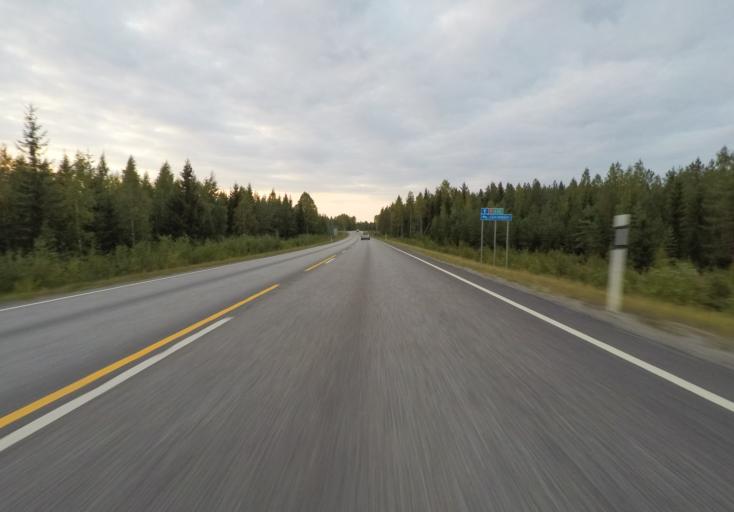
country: FI
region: Central Finland
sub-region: Jyvaeskylae
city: Hankasalmi
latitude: 62.3598
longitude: 26.5712
